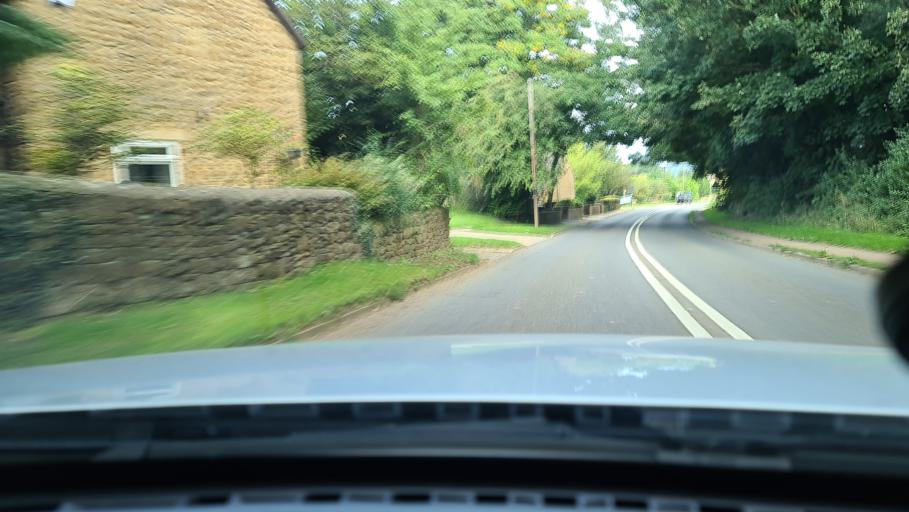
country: GB
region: England
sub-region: Oxfordshire
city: Hanwell
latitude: 52.0716
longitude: -1.3742
